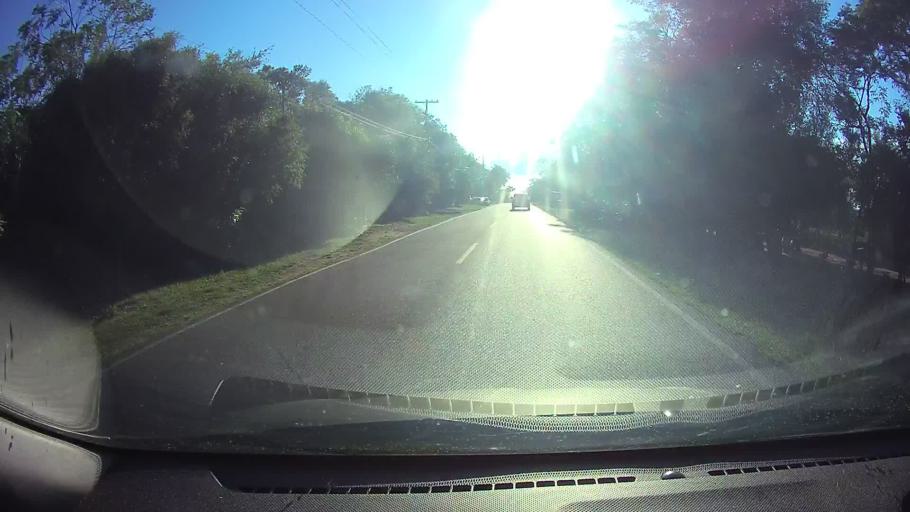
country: PY
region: Cordillera
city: Emboscada
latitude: -25.2029
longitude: -57.3346
